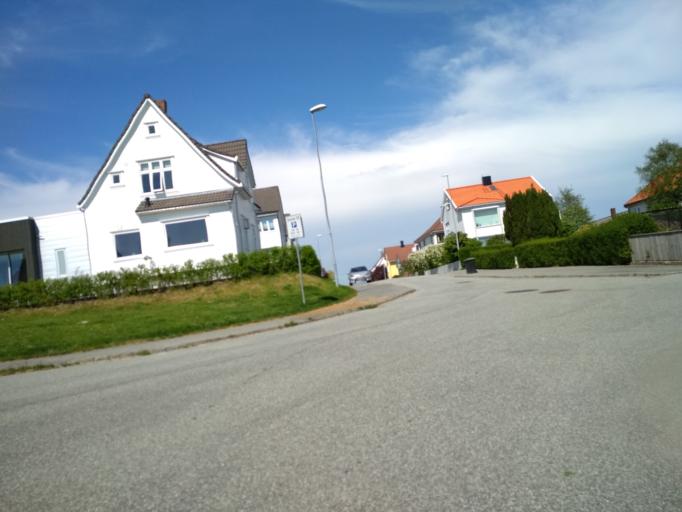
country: NO
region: Rogaland
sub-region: Stavanger
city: Stavanger
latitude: 58.9562
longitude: 5.7333
